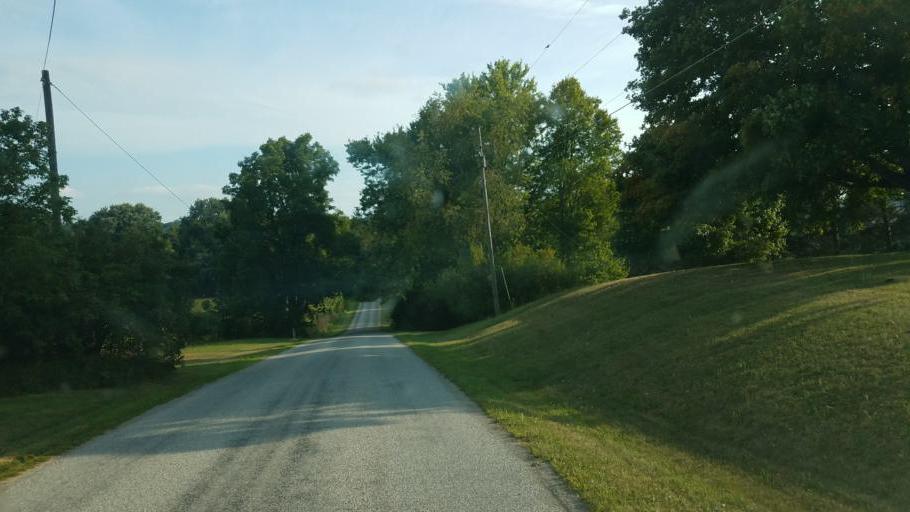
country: US
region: Ohio
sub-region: Sandusky County
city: Bellville
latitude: 40.6117
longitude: -82.4810
